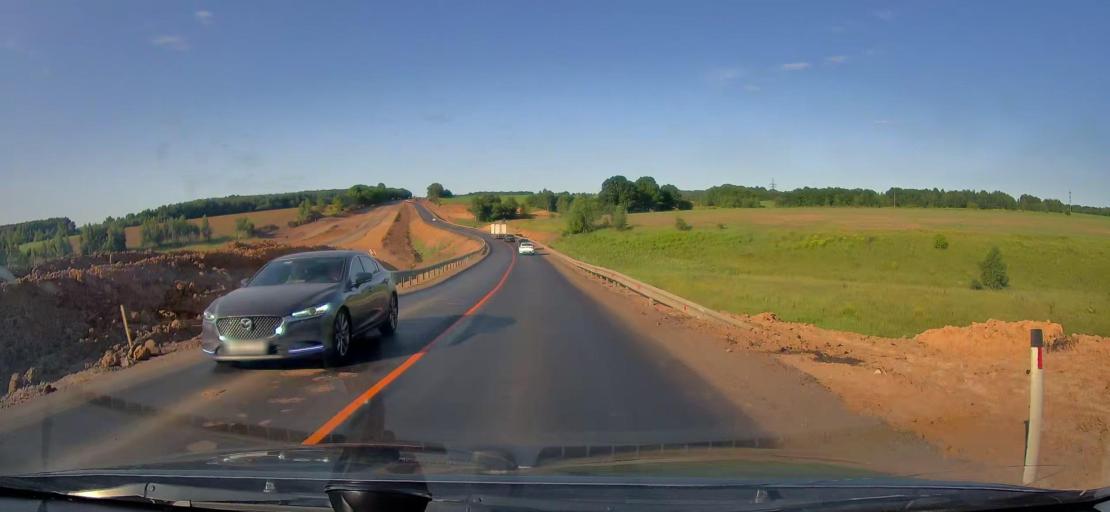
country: RU
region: Tula
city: Bol'shoye Skuratovo
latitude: 53.4158
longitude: 36.7815
